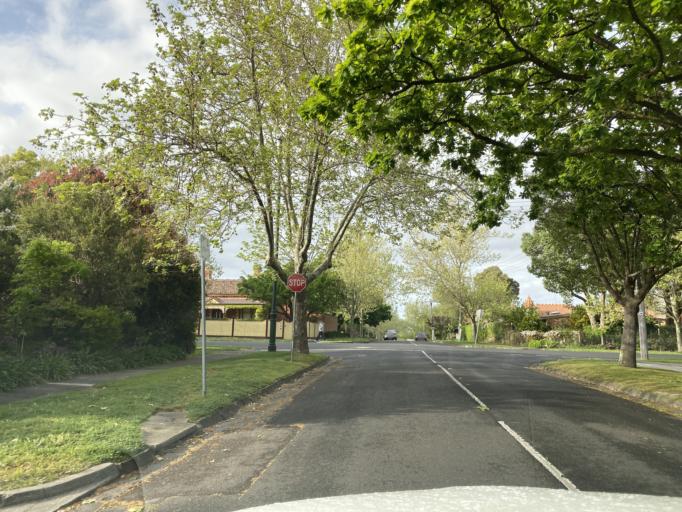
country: AU
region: Victoria
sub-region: Whitehorse
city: Surrey Hills
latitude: -37.8283
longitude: 145.0936
